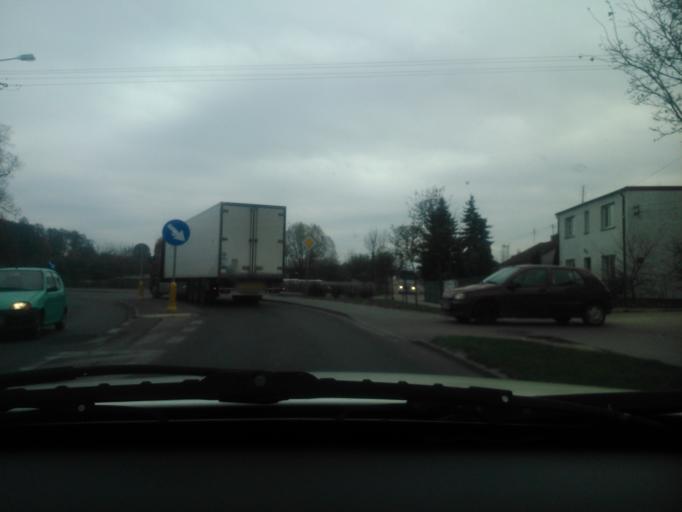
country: PL
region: Masovian Voivodeship
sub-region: Powiat mlawski
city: Szydlowo
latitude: 53.0802
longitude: 20.4480
